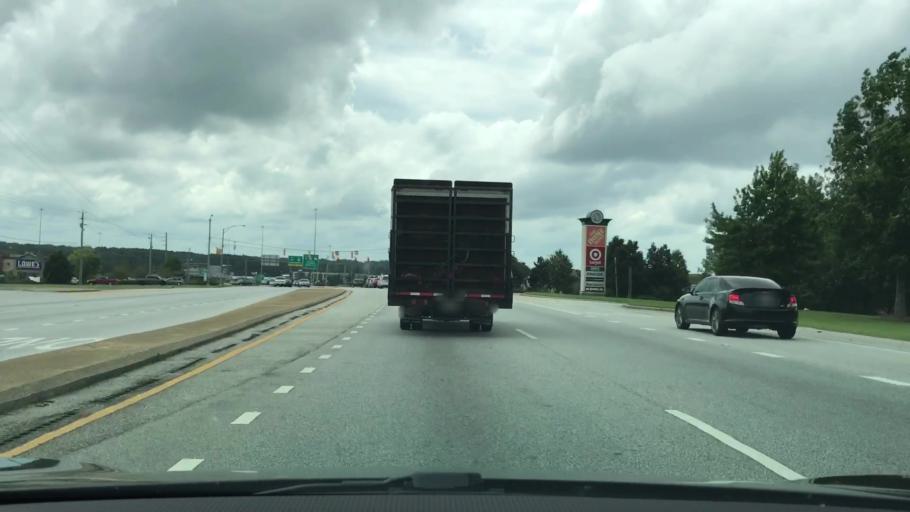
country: US
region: Alabama
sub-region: Lee County
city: Opelika
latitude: 32.6218
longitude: -85.4048
